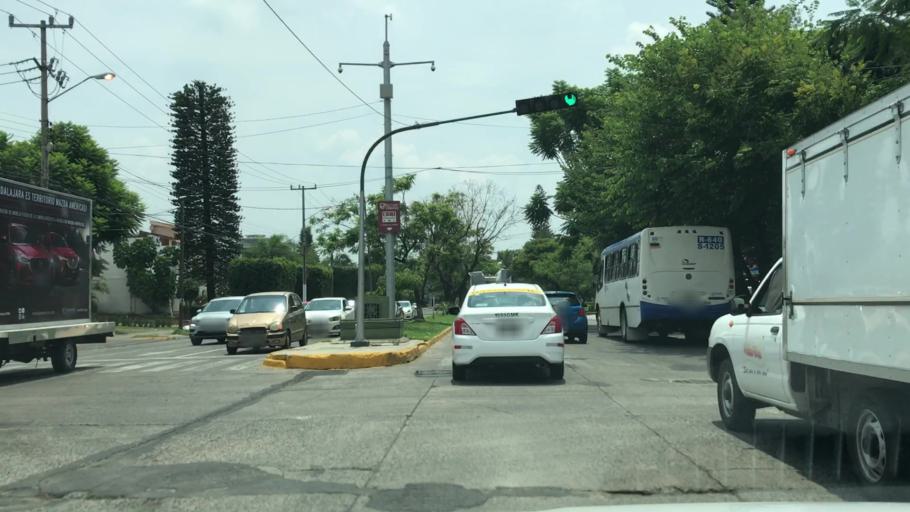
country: MX
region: Jalisco
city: Guadalajara
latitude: 20.6507
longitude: -103.4121
